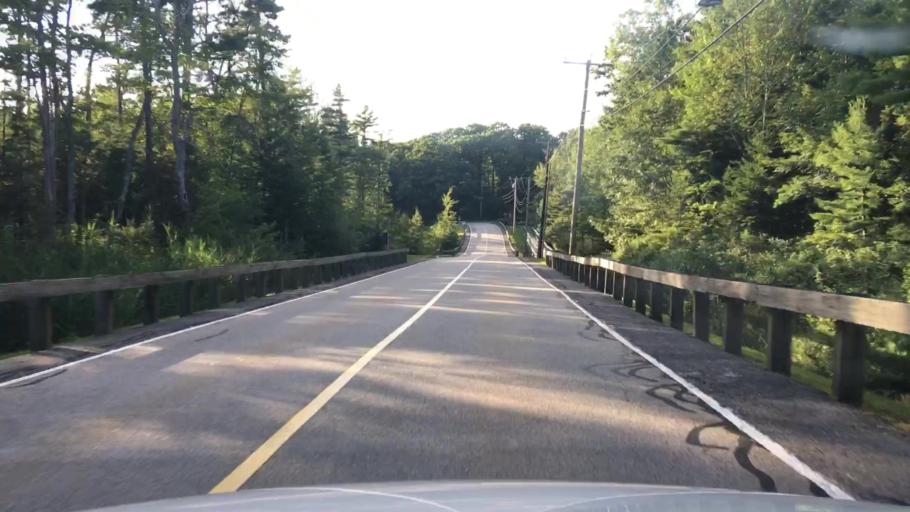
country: US
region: Maine
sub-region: Cumberland County
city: Scarborough
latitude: 43.5617
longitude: -70.2885
